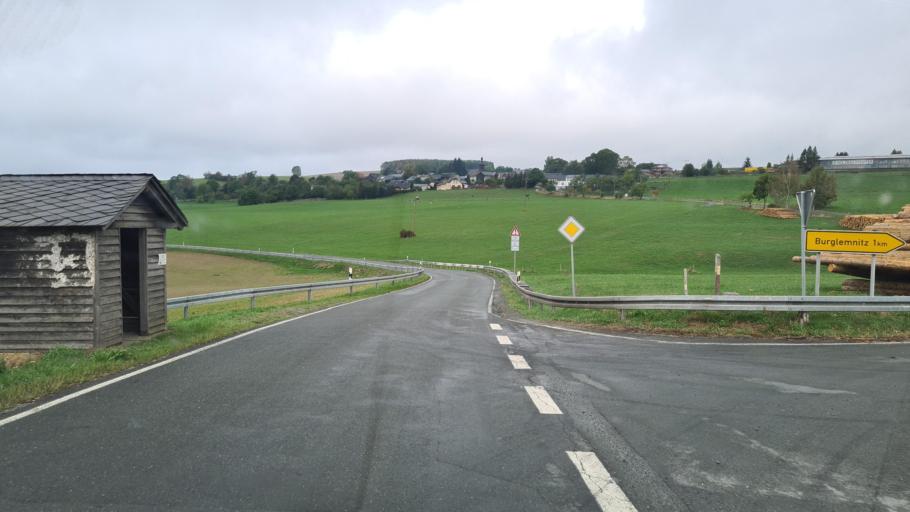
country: DE
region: Thuringia
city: Wurzbach
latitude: 50.5302
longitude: 11.5194
